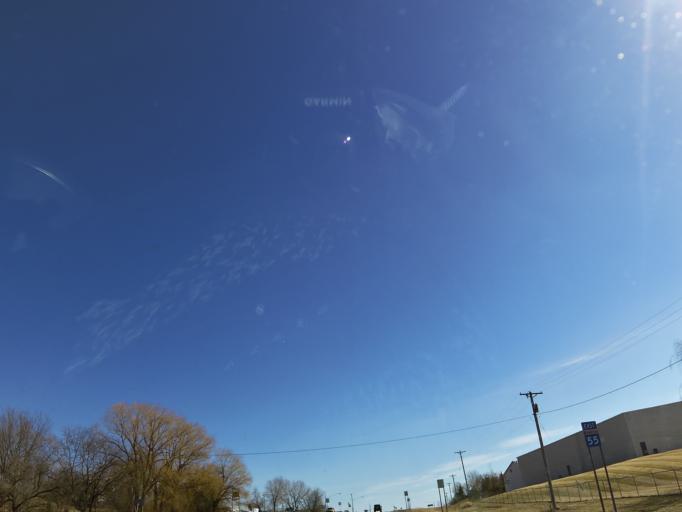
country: US
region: Minnesota
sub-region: Wright County
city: Rockford
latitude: 45.0849
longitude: -93.7325
